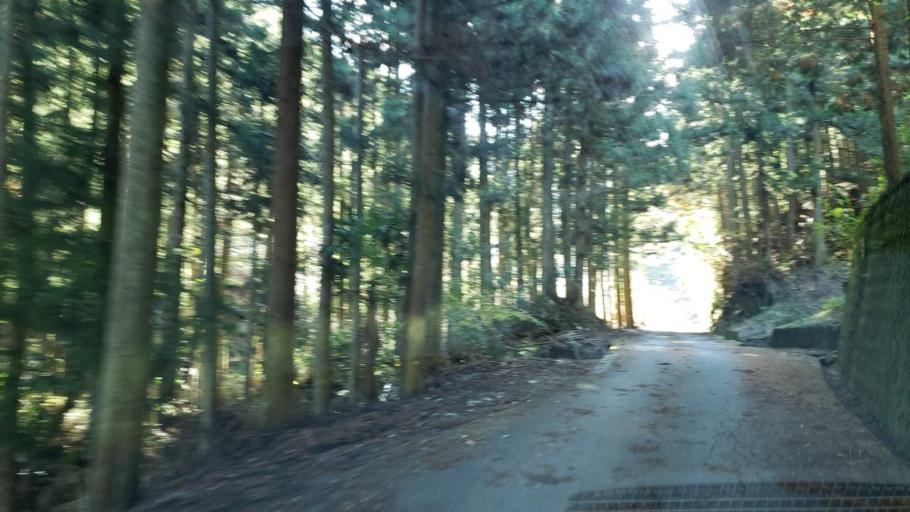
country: JP
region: Tokushima
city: Ikedacho
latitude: 33.9868
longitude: 133.9803
